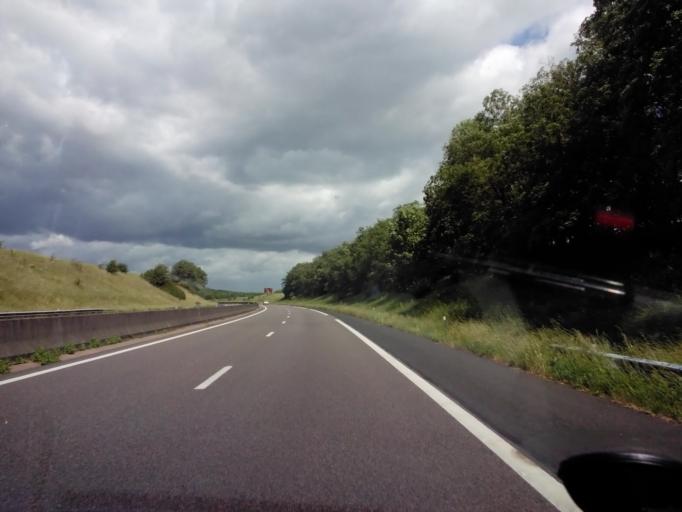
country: FR
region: Lorraine
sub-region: Departement des Vosges
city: Bulgneville
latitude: 48.2301
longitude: 5.8595
